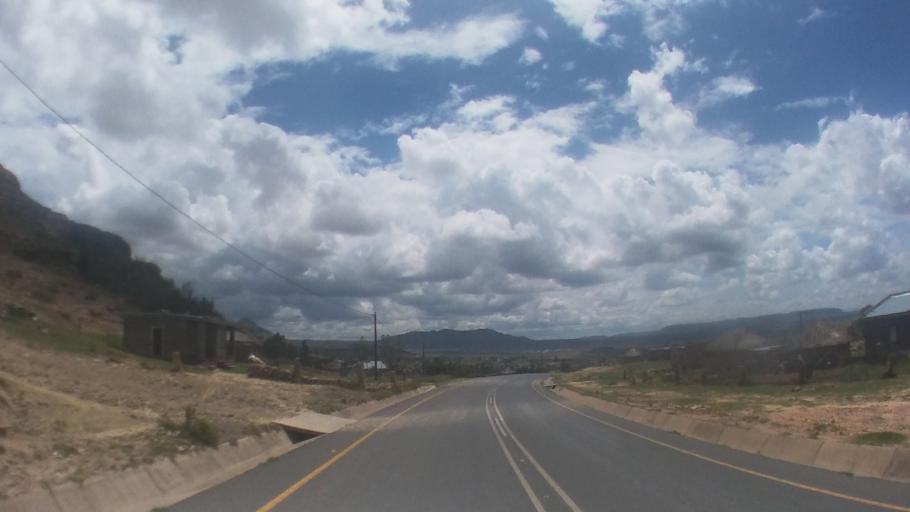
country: LS
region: Maseru
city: Maseru
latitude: -29.4256
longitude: 27.4692
